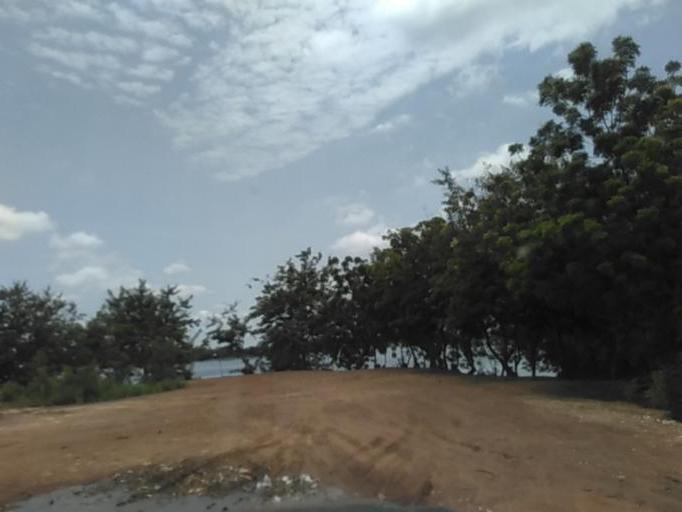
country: GH
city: Akropong
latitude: 6.0377
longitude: 0.3712
